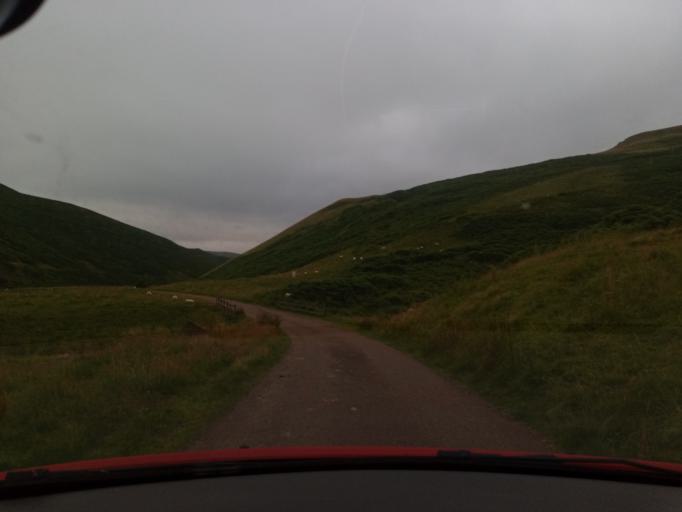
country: GB
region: England
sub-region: Northumberland
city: Rochester
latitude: 55.3695
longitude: -2.2137
